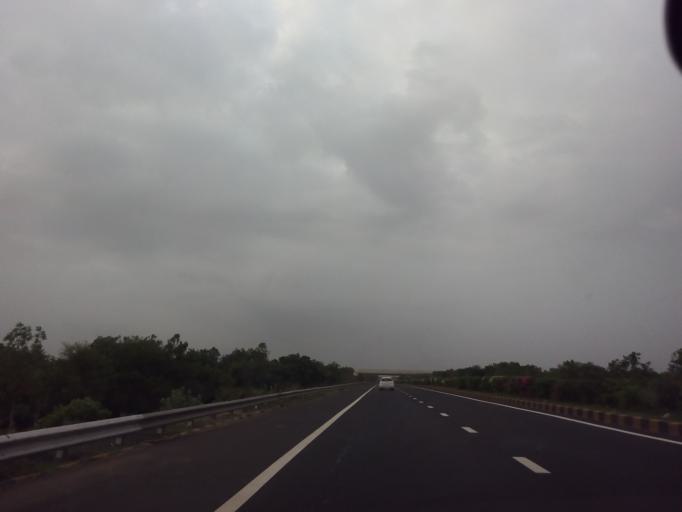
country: IN
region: Gujarat
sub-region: Kheda
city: Mahemdavad
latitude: 22.8693
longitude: 72.8034
